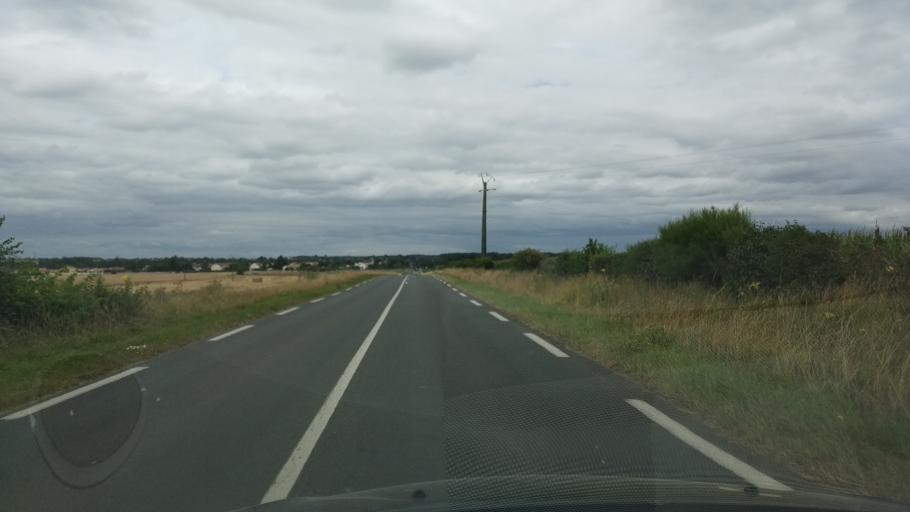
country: FR
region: Poitou-Charentes
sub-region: Departement de la Vienne
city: Roches-Premarie-Andille
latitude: 46.4713
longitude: 0.3685
